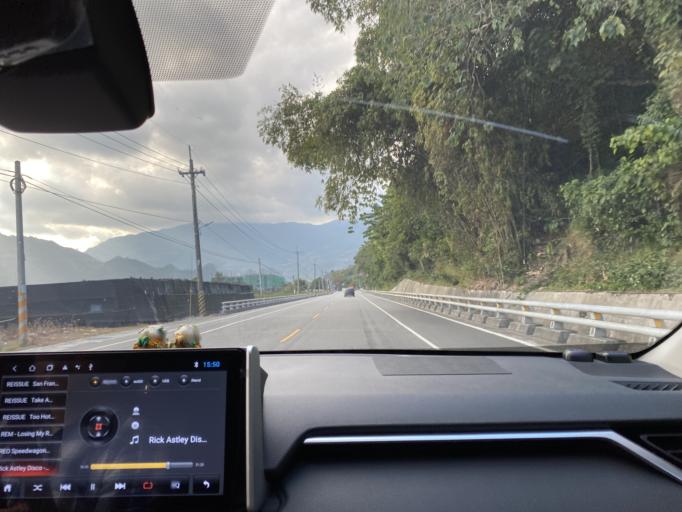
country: TW
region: Taiwan
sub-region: Taitung
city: Taitung
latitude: 22.8975
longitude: 121.1156
